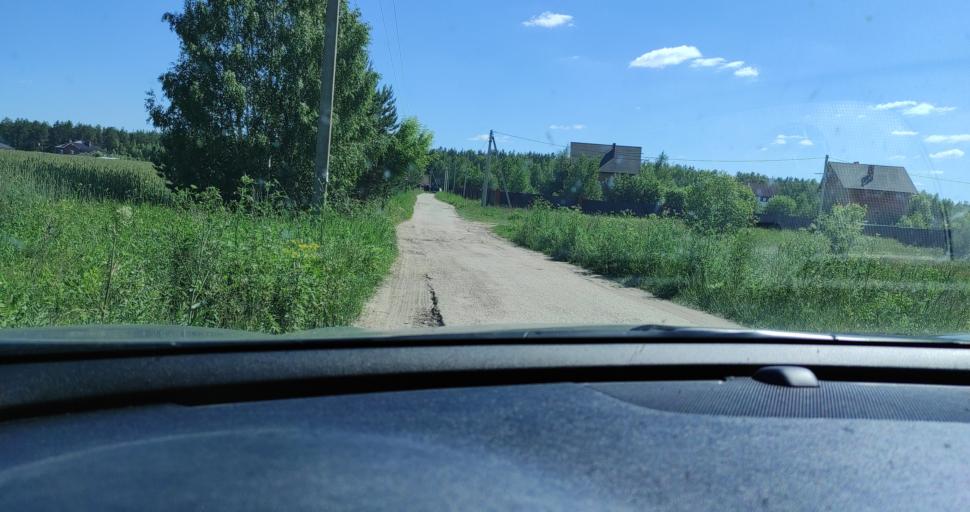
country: RU
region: Rjazan
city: Murmino
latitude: 54.5638
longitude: 40.0975
